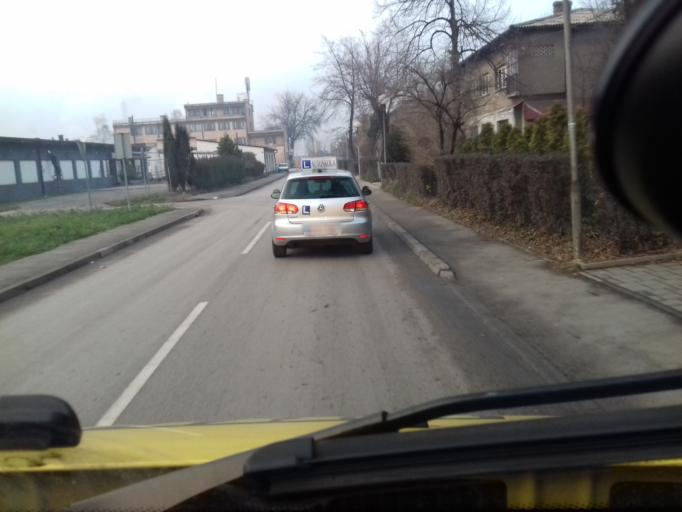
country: BA
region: Federation of Bosnia and Herzegovina
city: Zenica
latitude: 44.2078
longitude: 17.9048
